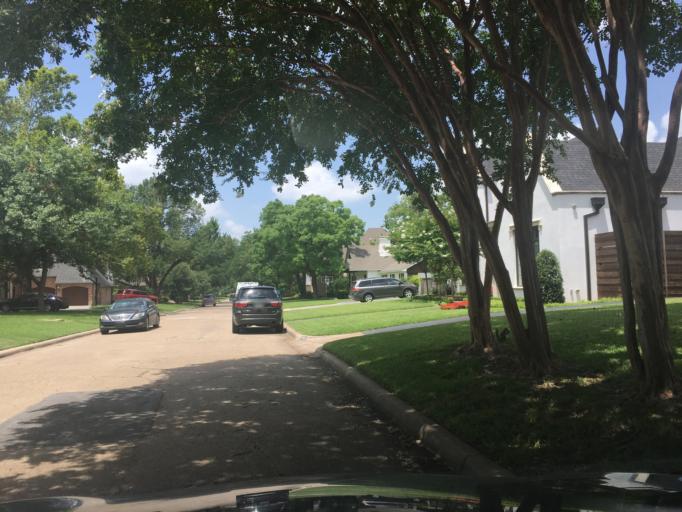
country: US
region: Texas
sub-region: Dallas County
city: University Park
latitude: 32.8791
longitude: -96.7880
